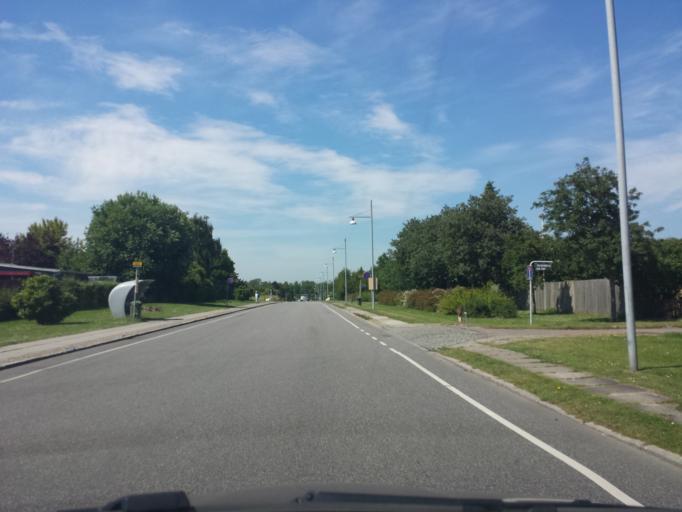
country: DK
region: Capital Region
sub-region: Glostrup Kommune
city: Glostrup
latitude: 55.7011
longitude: 12.4032
